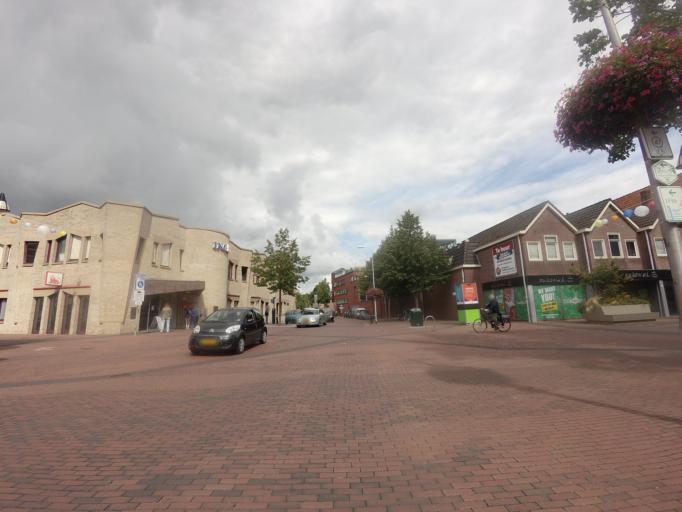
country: NL
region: Drenthe
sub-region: Gemeente Meppel
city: Meppel
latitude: 52.6994
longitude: 6.1887
